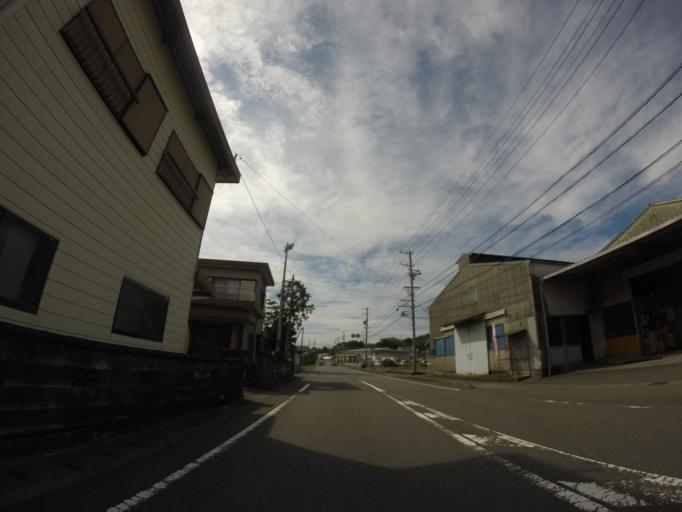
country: JP
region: Shizuoka
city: Shimada
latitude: 34.7544
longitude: 138.2082
